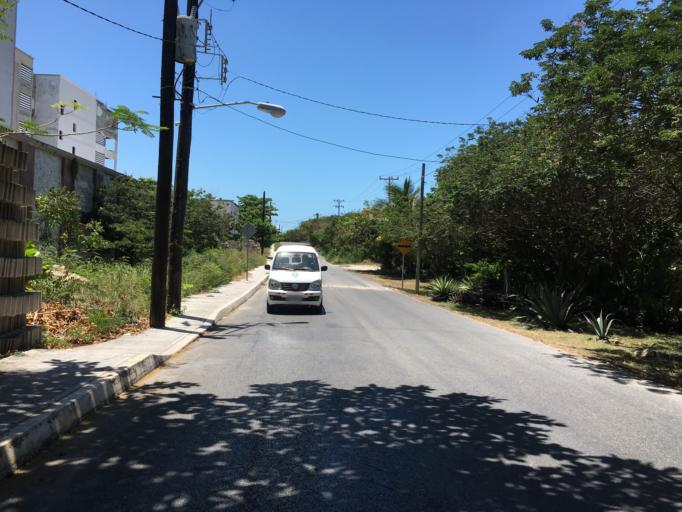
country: MX
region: Quintana Roo
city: Isla Mujeres
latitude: 21.2098
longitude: -86.7200
